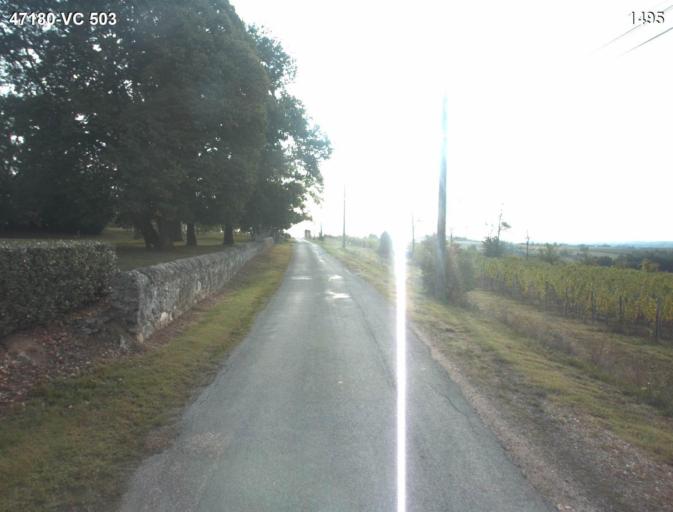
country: FR
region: Aquitaine
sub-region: Departement du Lot-et-Garonne
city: Sainte-Colombe-en-Bruilhois
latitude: 44.1726
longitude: 0.4375
